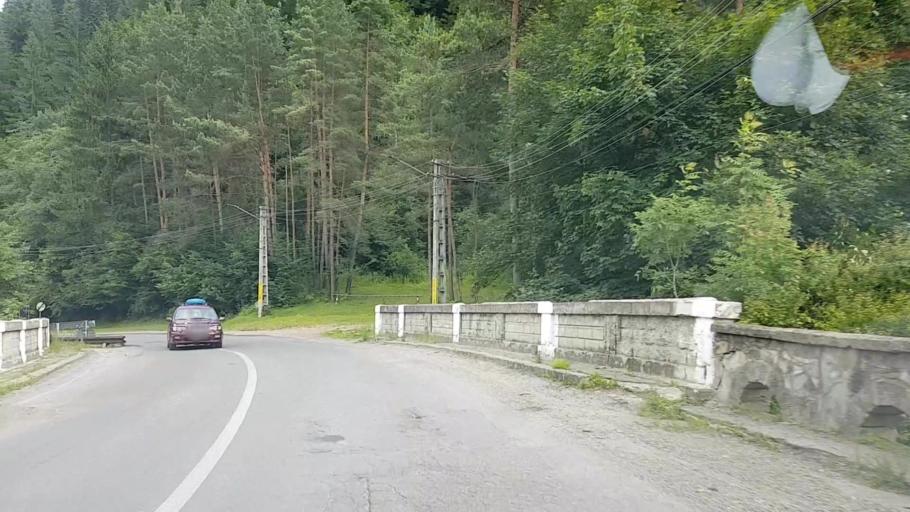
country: RO
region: Neamt
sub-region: Comuna Bicaz
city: Dodeni
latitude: 46.9384
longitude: 26.0833
